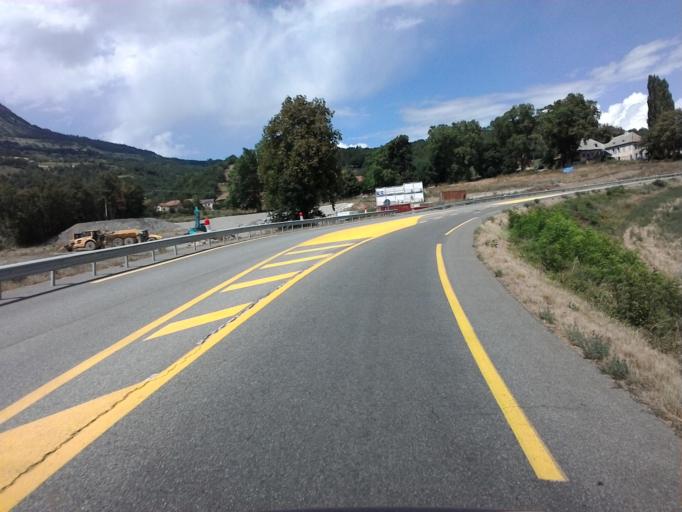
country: FR
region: Provence-Alpes-Cote d'Azur
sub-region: Departement des Hautes-Alpes
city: Gap
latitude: 44.5752
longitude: 6.0742
